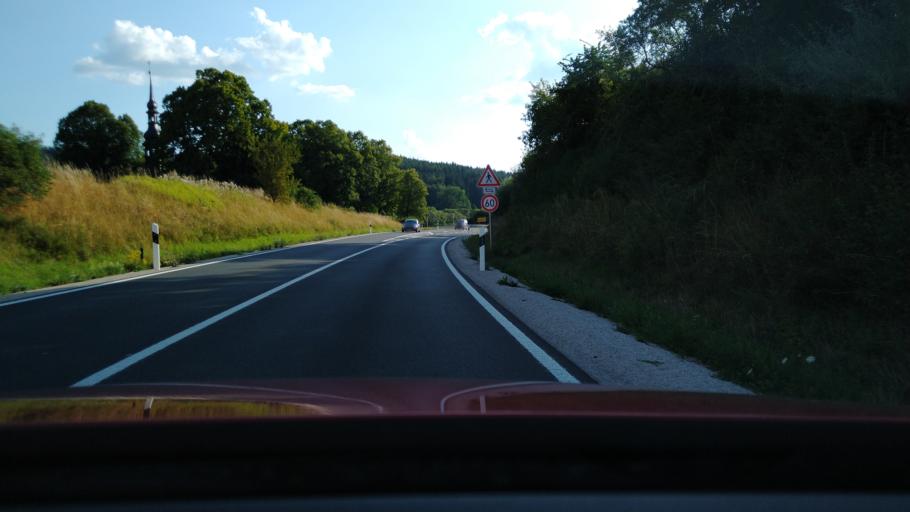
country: DE
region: Bavaria
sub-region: Upper Franconia
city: Glashutten
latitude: 49.9180
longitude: 11.3968
